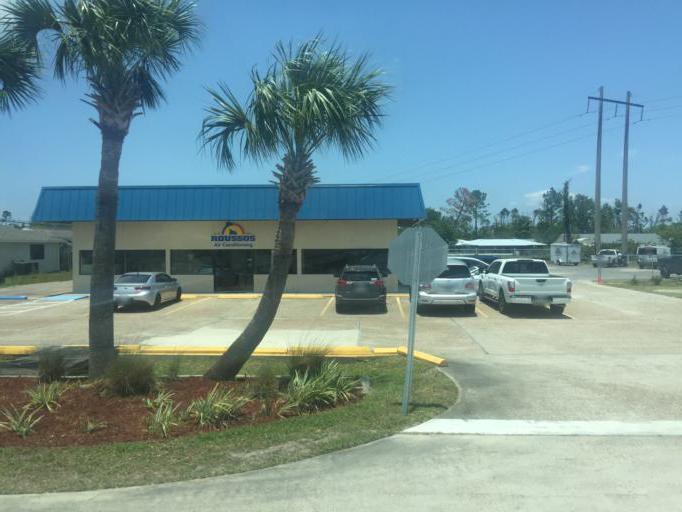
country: US
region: Florida
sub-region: Bay County
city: Lynn Haven
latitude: 30.2188
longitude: -85.6593
